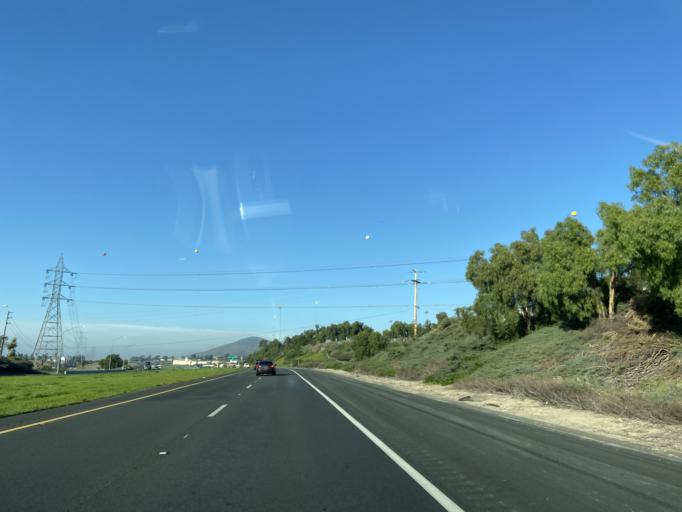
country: US
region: California
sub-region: San Diego County
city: Bonita
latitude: 32.6381
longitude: -116.9707
